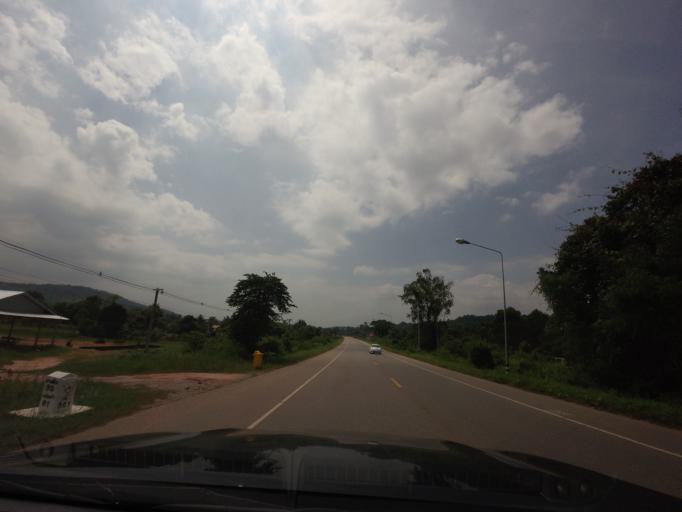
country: TH
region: Loei
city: Phu Ruea
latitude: 17.4474
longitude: 101.3401
